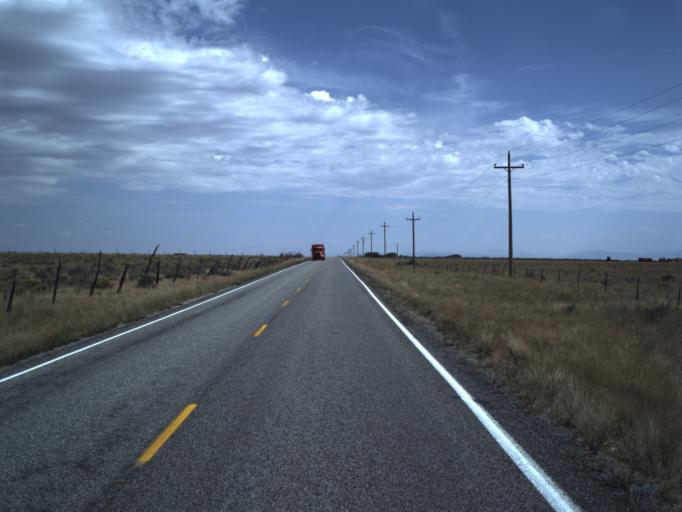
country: US
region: Idaho
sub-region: Cassia County
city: Burley
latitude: 41.8171
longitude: -113.2944
